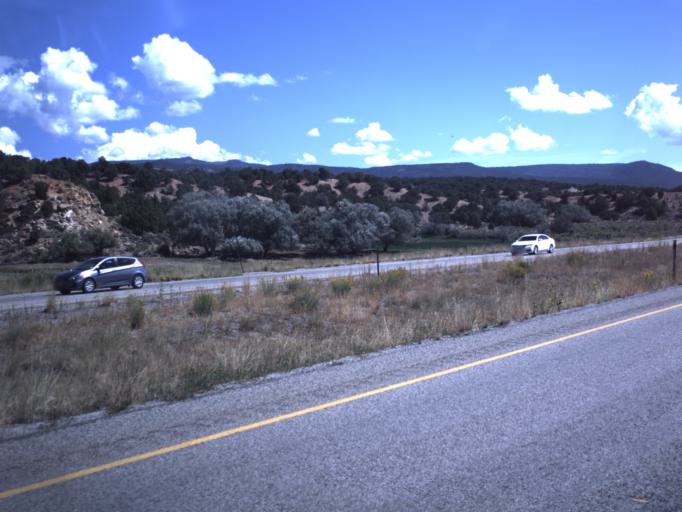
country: US
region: Utah
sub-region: Sevier County
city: Salina
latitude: 38.9187
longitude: -111.7502
